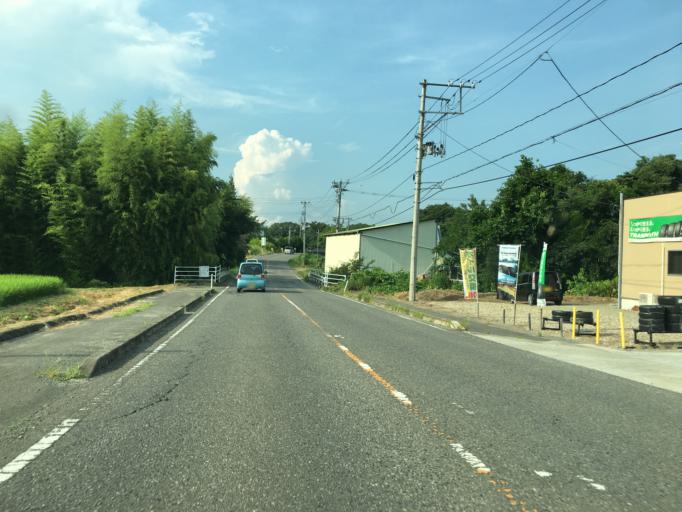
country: JP
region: Fukushima
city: Miharu
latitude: 37.4482
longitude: 140.4275
